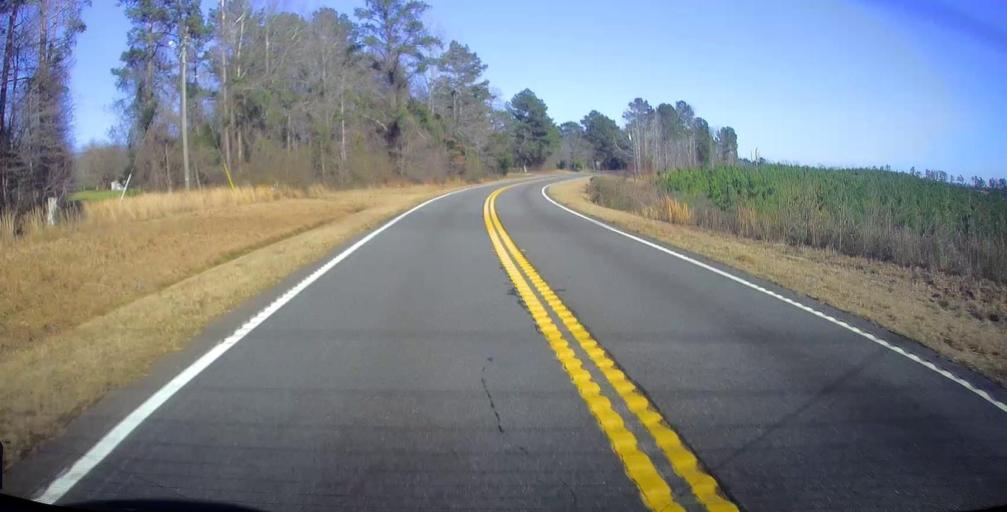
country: US
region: Georgia
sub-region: Talbot County
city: Talbotton
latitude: 32.6468
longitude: -84.4243
